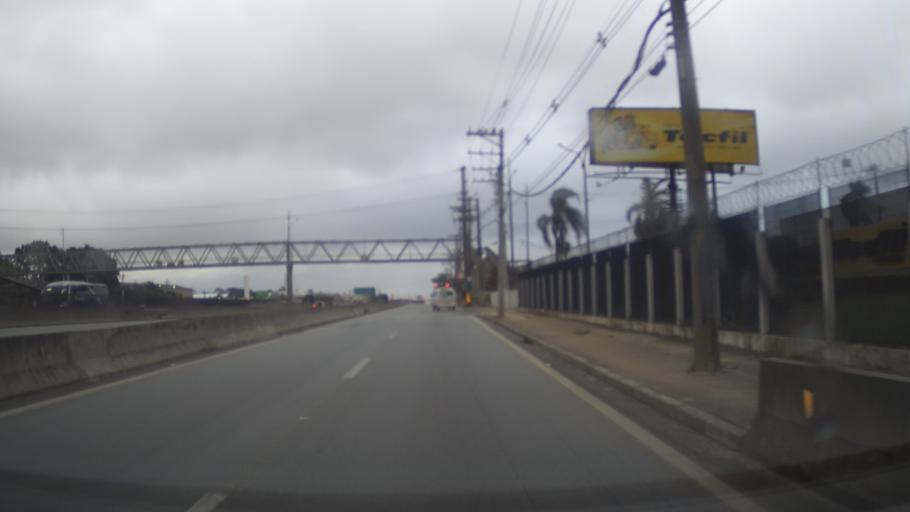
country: BR
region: Sao Paulo
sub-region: Guarulhos
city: Guarulhos
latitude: -23.4432
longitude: -46.4463
